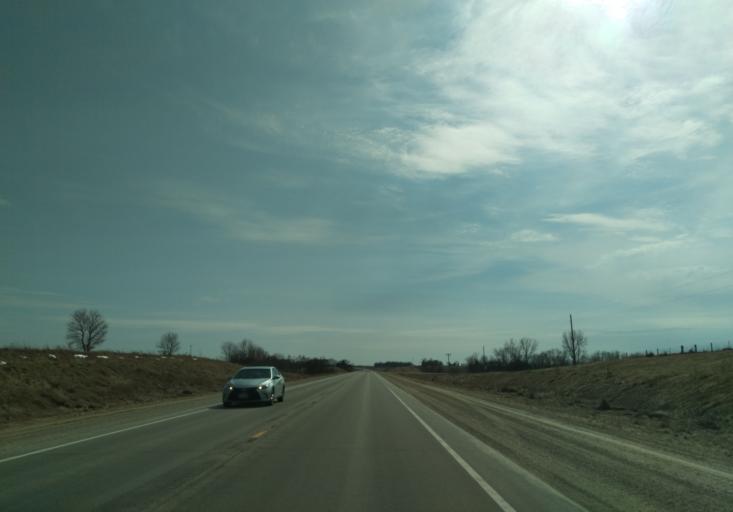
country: US
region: Minnesota
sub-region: Fillmore County
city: Harmony
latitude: 43.4674
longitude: -91.8699
